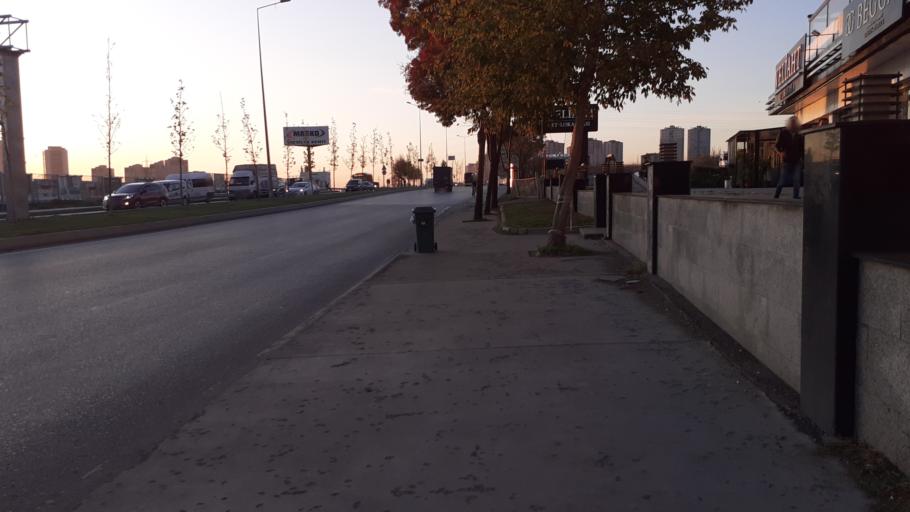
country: TR
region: Istanbul
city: Basaksehir
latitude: 41.0660
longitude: 28.7866
